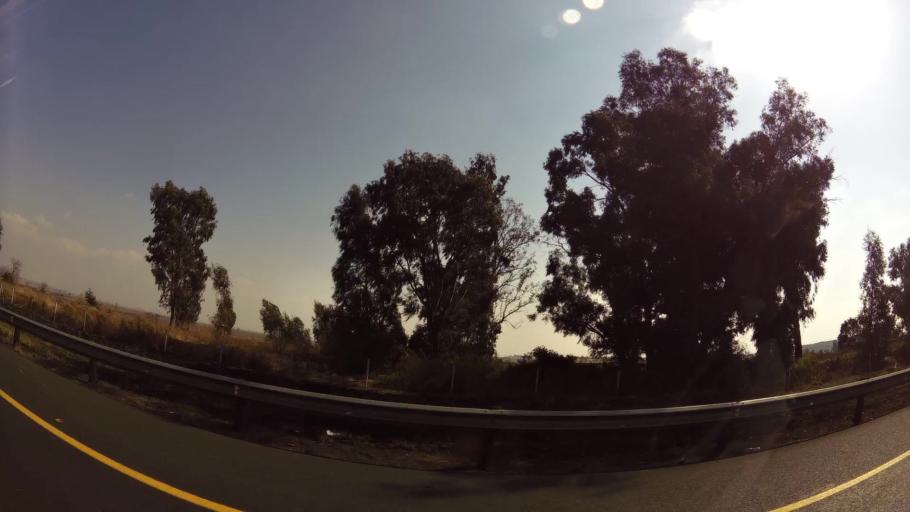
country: ZA
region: Gauteng
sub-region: Ekurhuleni Metropolitan Municipality
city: Springs
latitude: -26.1601
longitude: 28.5190
